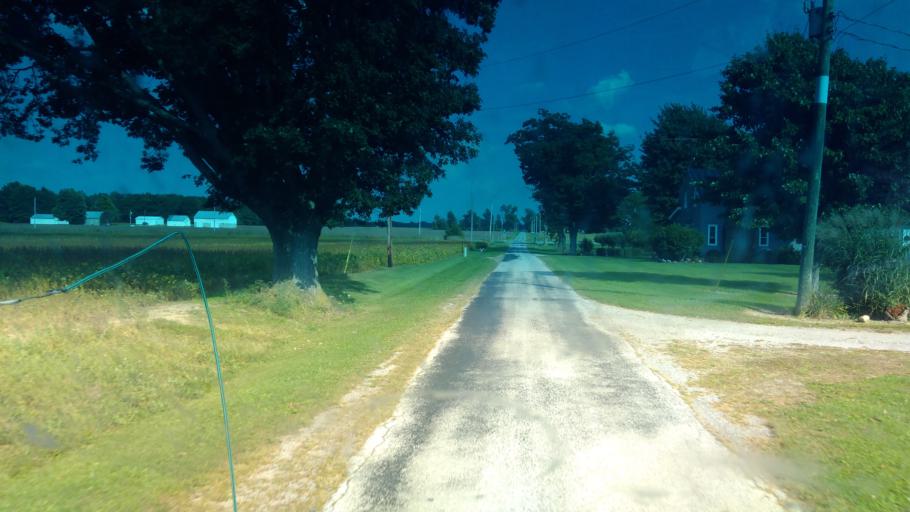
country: US
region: Ohio
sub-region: Hardin County
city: Forest
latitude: 40.8189
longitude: -83.5787
